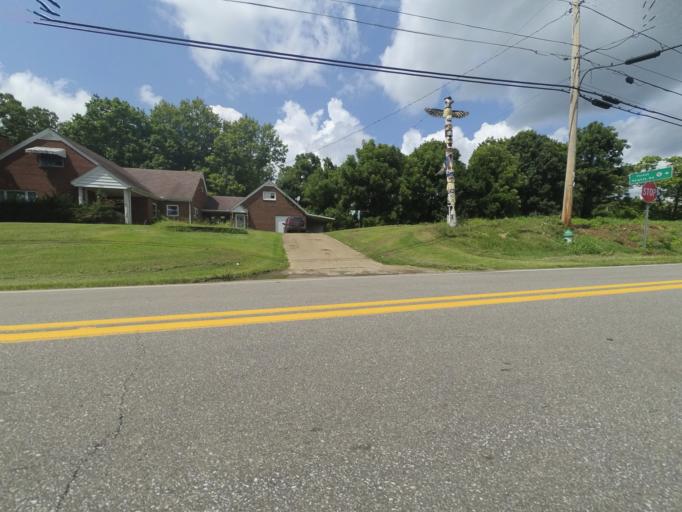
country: US
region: West Virginia
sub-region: Cabell County
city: Pea Ridge
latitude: 38.4098
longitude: -82.3409
